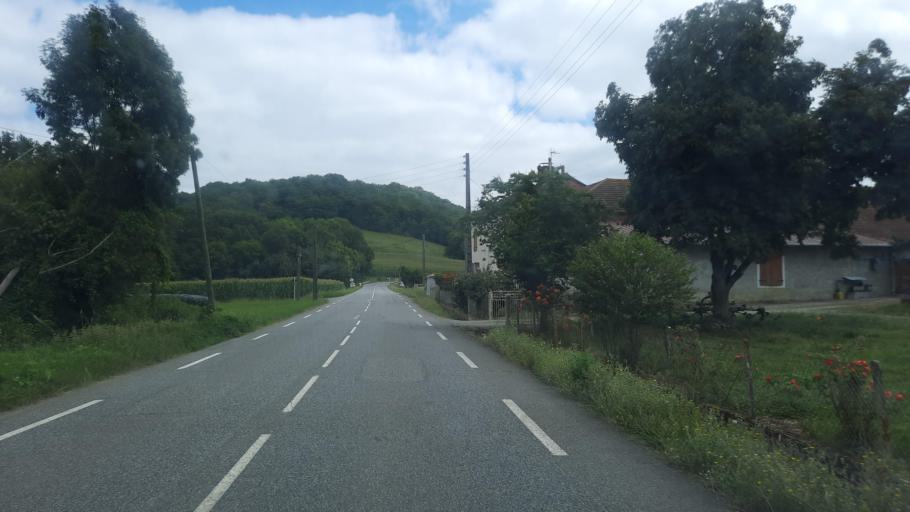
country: FR
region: Midi-Pyrenees
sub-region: Departement des Hautes-Pyrenees
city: Trie-sur-Baise
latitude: 43.3051
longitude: 0.2669
